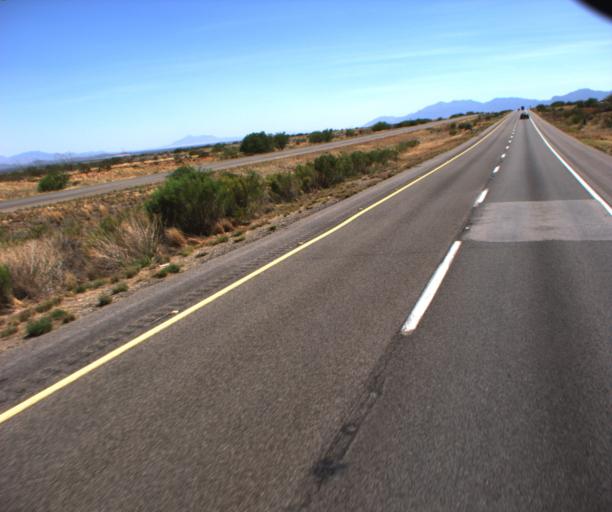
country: US
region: Arizona
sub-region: Cochise County
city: Huachuca City
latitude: 31.7906
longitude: -110.3503
